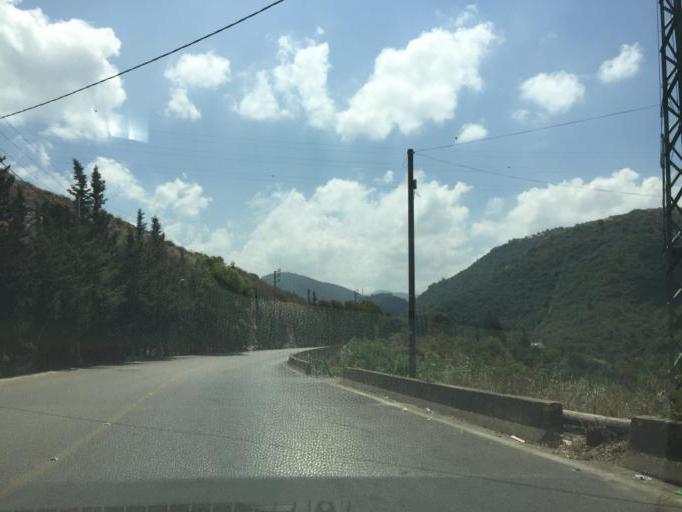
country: LB
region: Mont-Liban
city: Beit ed Dine
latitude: 33.7084
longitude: 35.4575
